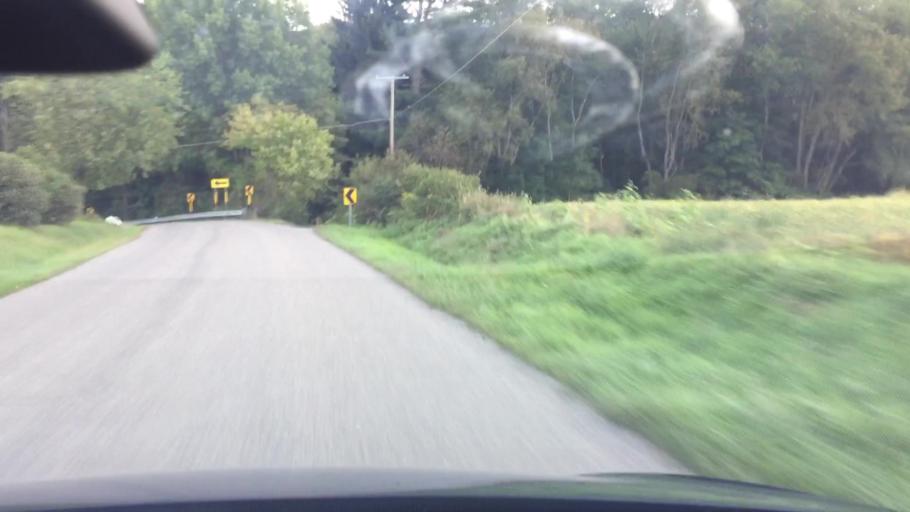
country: US
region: Pennsylvania
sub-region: Butler County
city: Oak Hills
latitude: 40.8110
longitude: -79.8915
